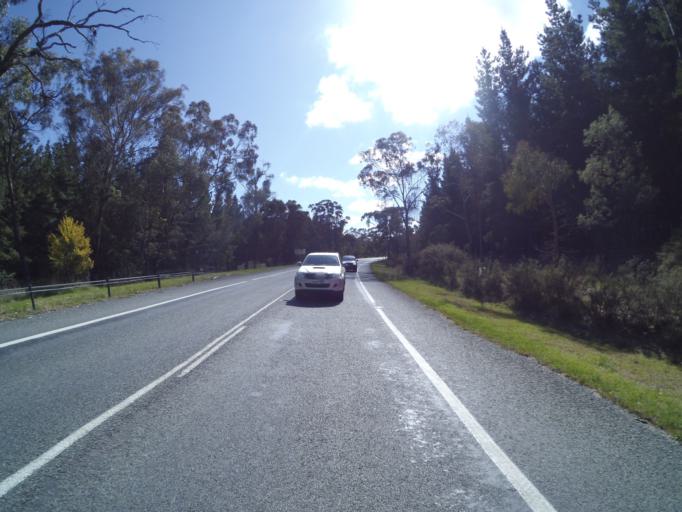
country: AU
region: New South Wales
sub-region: Queanbeyan
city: Queanbeyan
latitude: -35.2707
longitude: 149.2607
